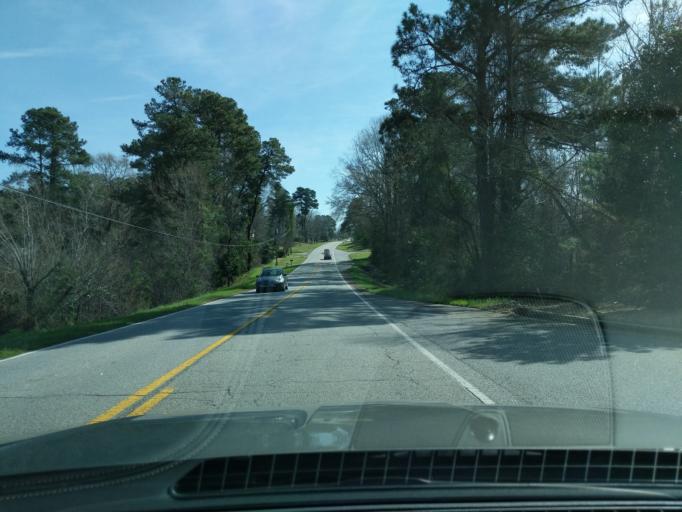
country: US
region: Georgia
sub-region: Columbia County
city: Evans
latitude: 33.5334
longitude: -82.1381
